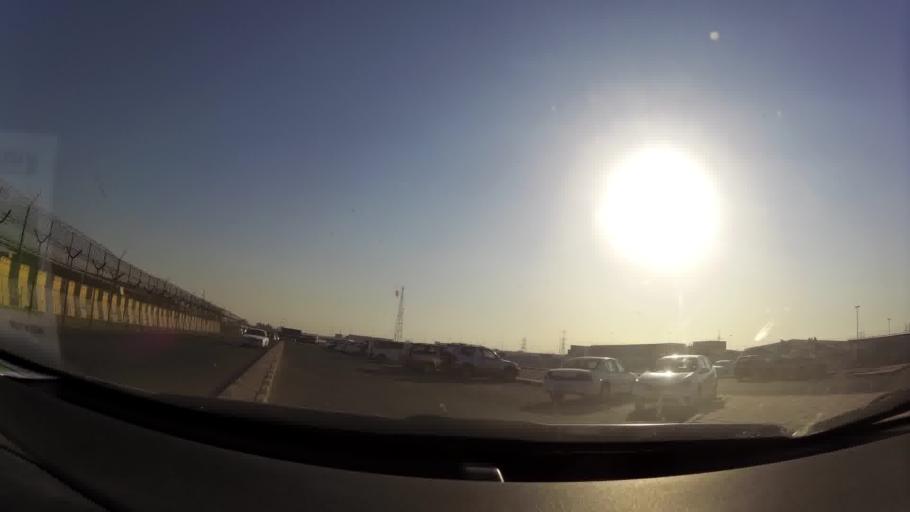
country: KW
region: Al Ahmadi
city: Al Fahahil
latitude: 29.0448
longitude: 48.1210
